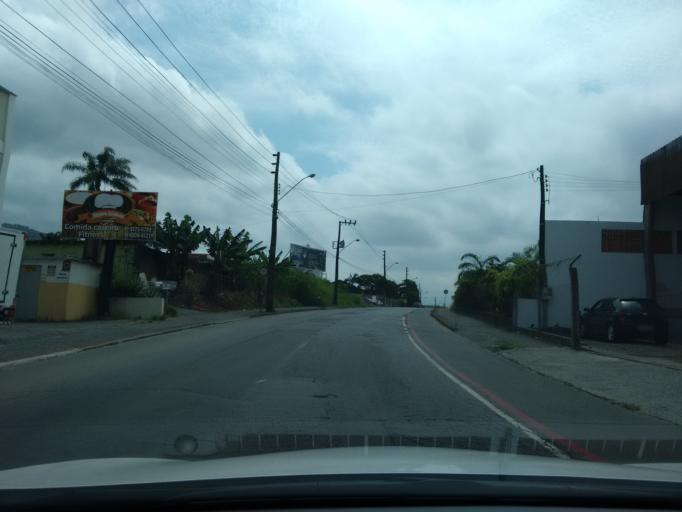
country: BR
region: Santa Catarina
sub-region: Jaragua Do Sul
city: Jaragua do Sul
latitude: -26.4891
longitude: -49.0580
